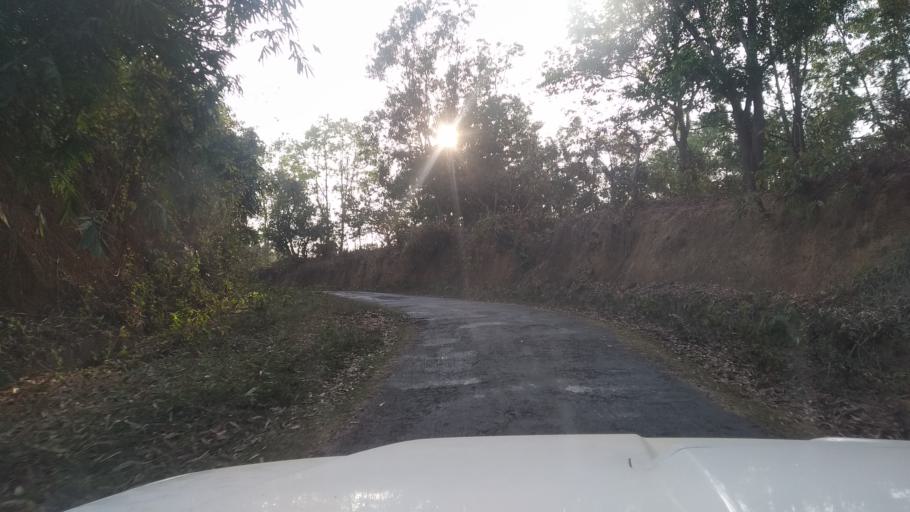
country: IN
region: Tripura
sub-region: West Tripura
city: Sonamura
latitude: 23.3385
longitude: 91.3160
